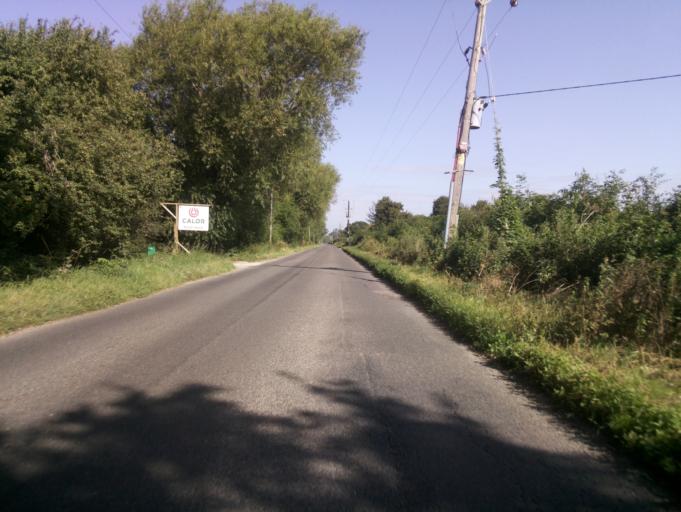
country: GB
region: England
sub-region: Oxfordshire
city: Bampton
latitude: 51.7142
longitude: -1.5254
